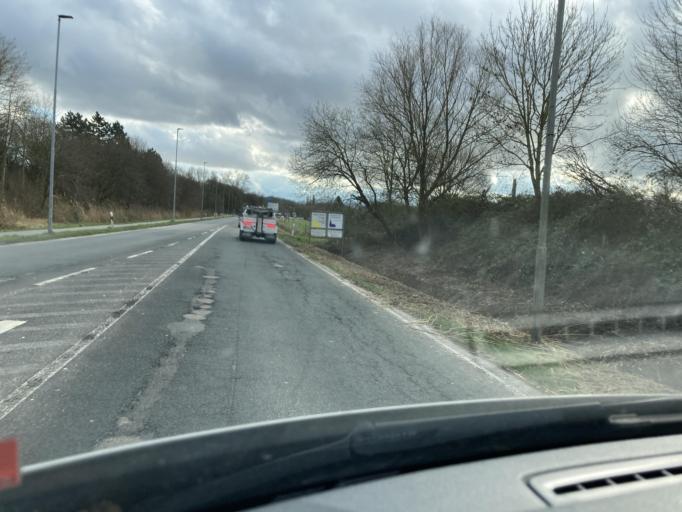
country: DE
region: Lower Saxony
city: Wilhelmshaven
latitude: 53.5524
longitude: 8.0832
